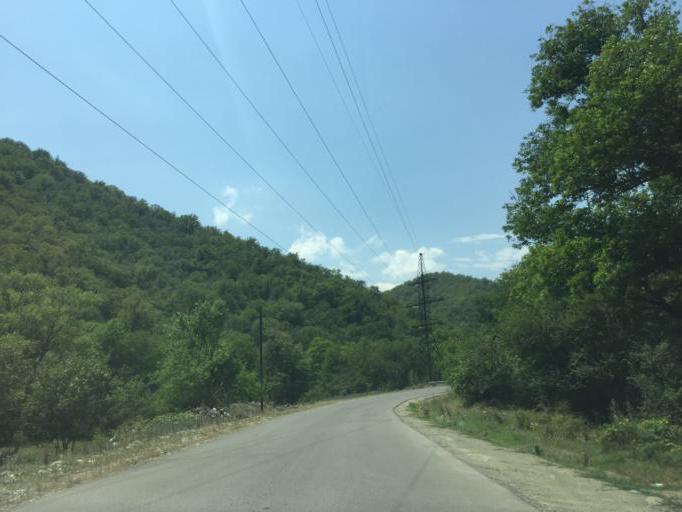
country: AZ
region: Kalbacar Rayonu
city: Kerbakhiar
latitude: 40.1339
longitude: 46.3811
